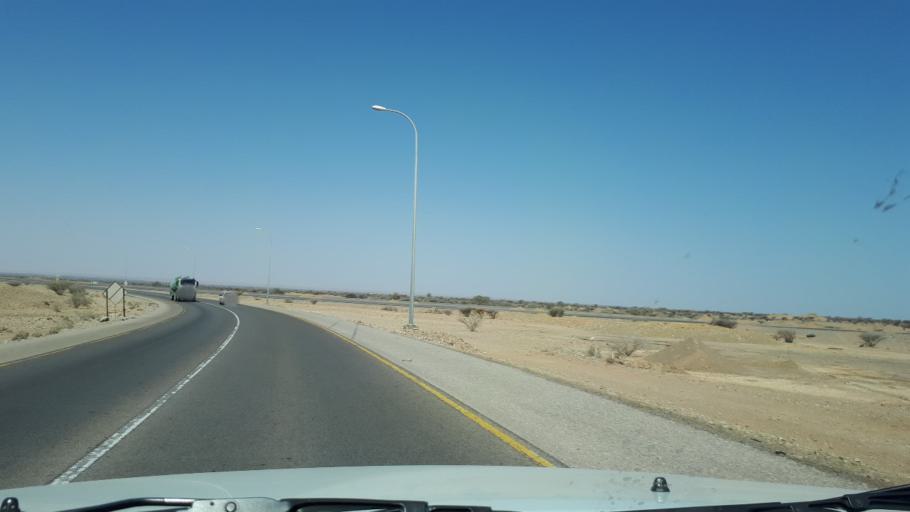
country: OM
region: Ash Sharqiyah
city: Sur
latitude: 22.3157
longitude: 59.2960
